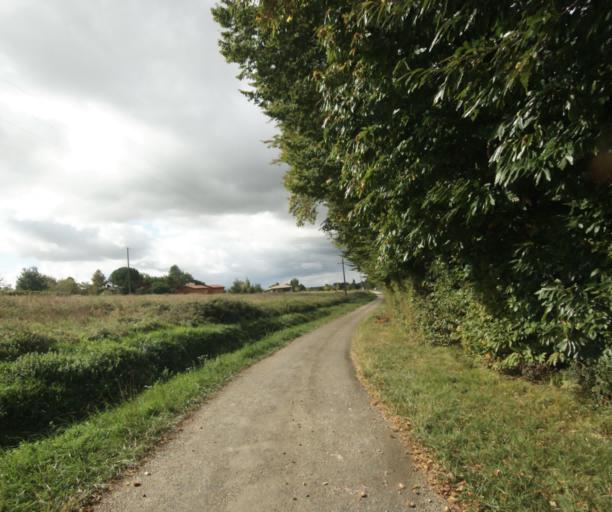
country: FR
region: Midi-Pyrenees
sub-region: Departement du Gers
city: Eauze
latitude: 43.8521
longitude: 0.0524
